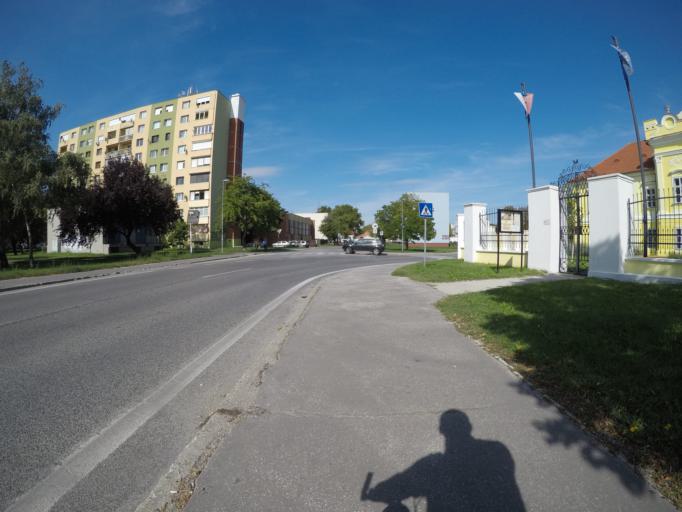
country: SK
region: Trnavsky
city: Dunajska Streda
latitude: 47.9939
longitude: 17.6216
